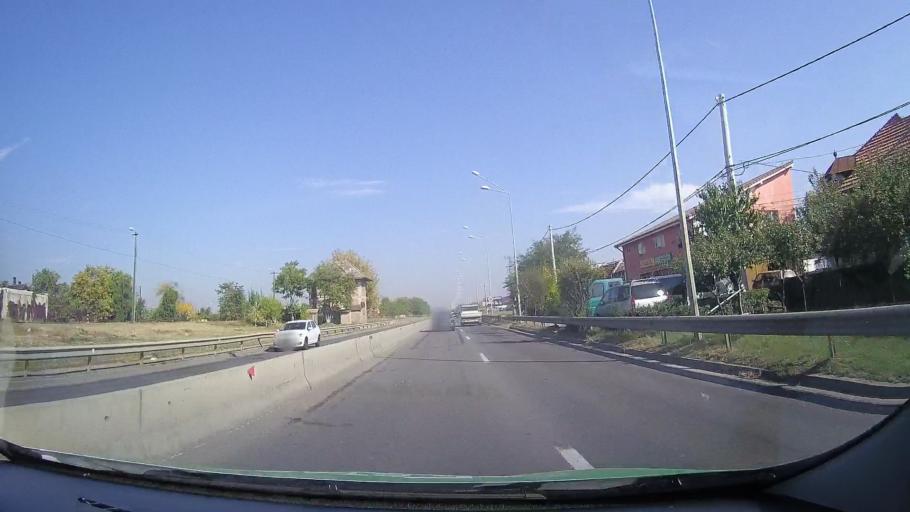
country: RO
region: Bihor
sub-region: Comuna Santandrei
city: Santandrei
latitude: 47.0553
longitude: 21.8902
